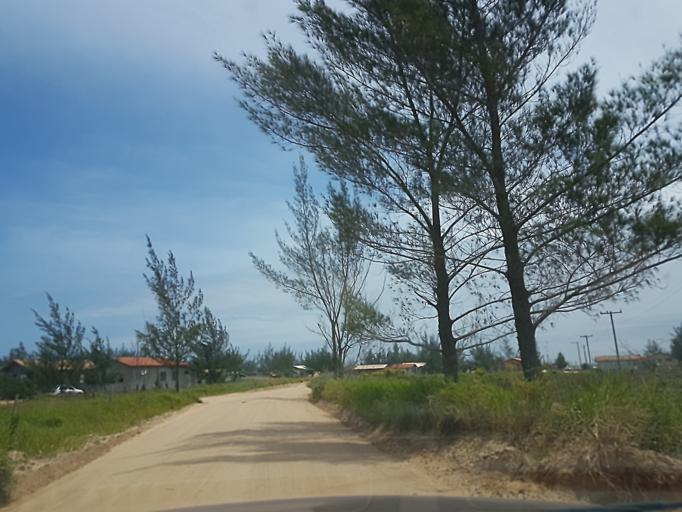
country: BR
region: Santa Catarina
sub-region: Jaguaruna
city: Jaguaruna
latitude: -28.6589
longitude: -48.9594
